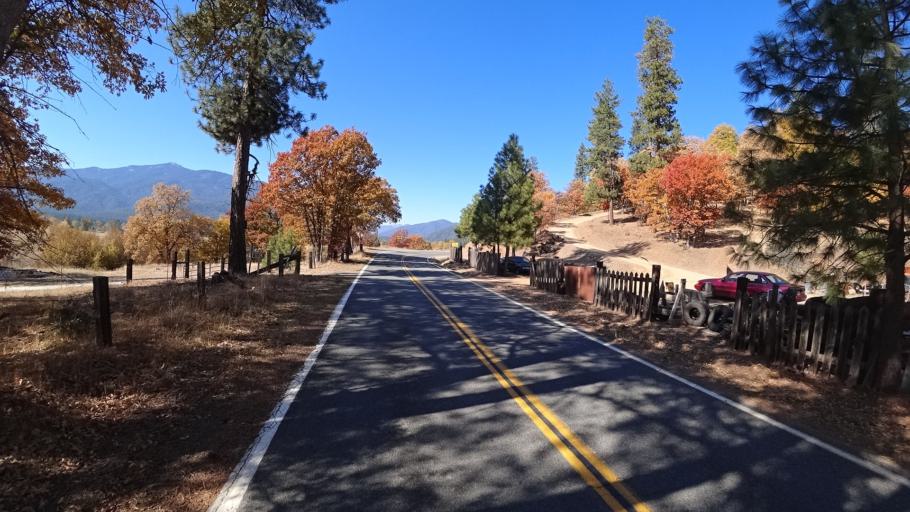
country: US
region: California
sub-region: Siskiyou County
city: Yreka
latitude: 41.6322
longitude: -122.9554
